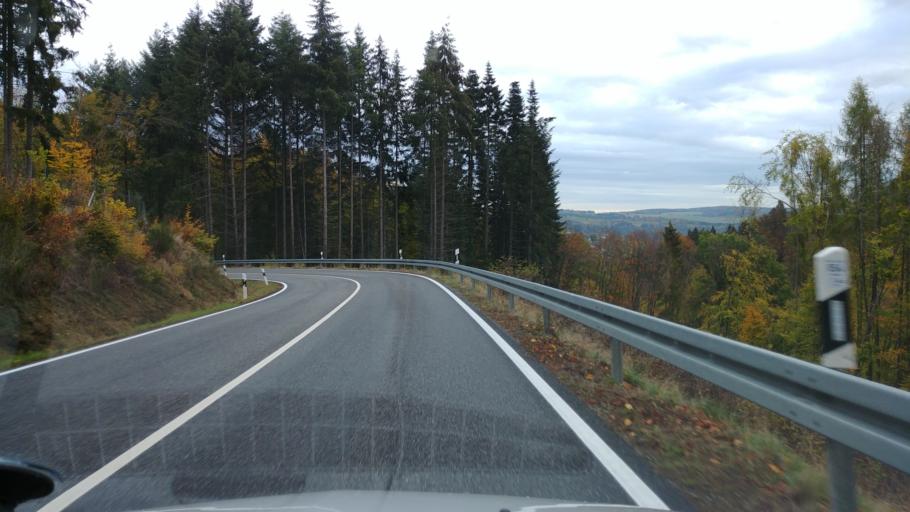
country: DE
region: Hesse
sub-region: Regierungsbezirk Darmstadt
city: Bad Schwalbach
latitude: 50.1331
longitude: 8.0513
